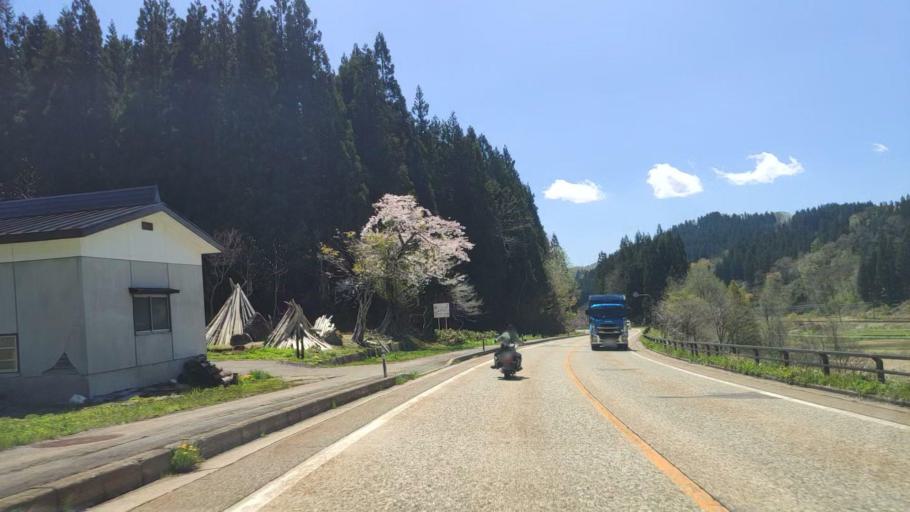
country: JP
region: Akita
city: Yuzawa
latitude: 38.9973
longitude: 140.3639
